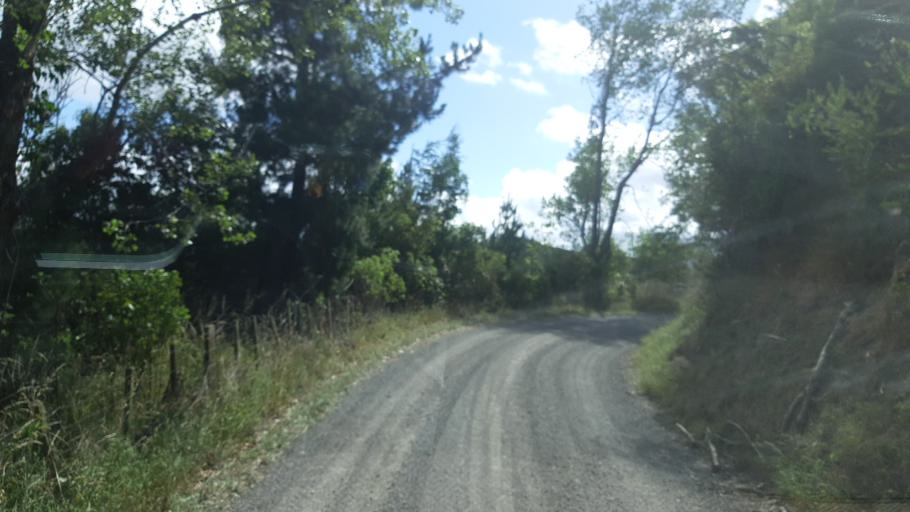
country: NZ
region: Manawatu-Wanganui
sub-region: Palmerston North City
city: Palmerston North
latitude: -40.1641
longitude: 175.7716
